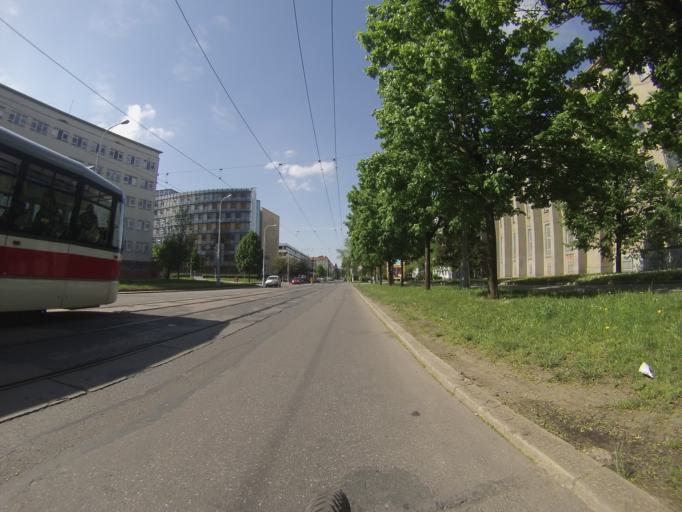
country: CZ
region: South Moravian
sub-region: Mesto Brno
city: Brno
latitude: 49.2080
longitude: 16.5954
